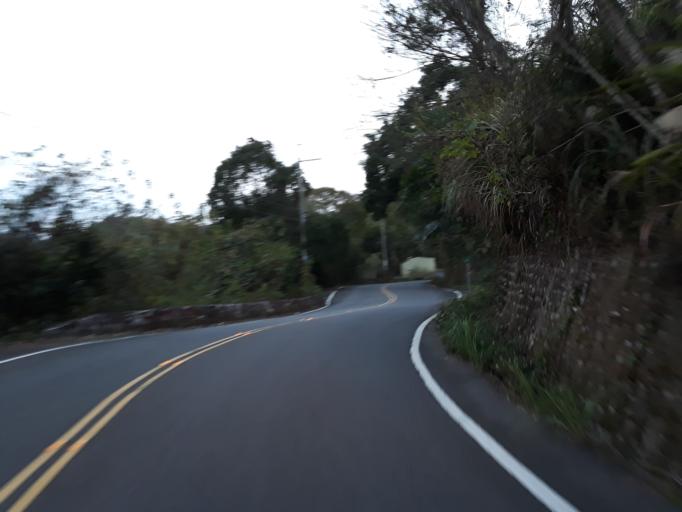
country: TW
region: Taiwan
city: Fengyuan
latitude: 24.3651
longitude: 120.8673
